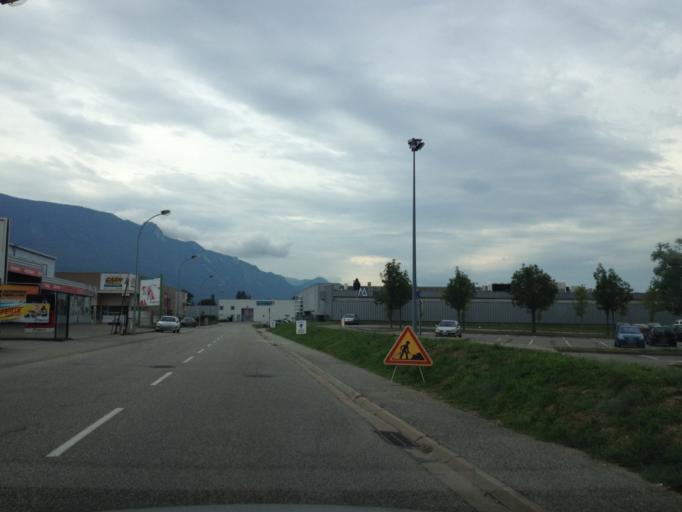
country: FR
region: Rhone-Alpes
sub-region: Departement de la Savoie
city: La Motte-Servolex
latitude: 45.6129
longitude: 5.8873
